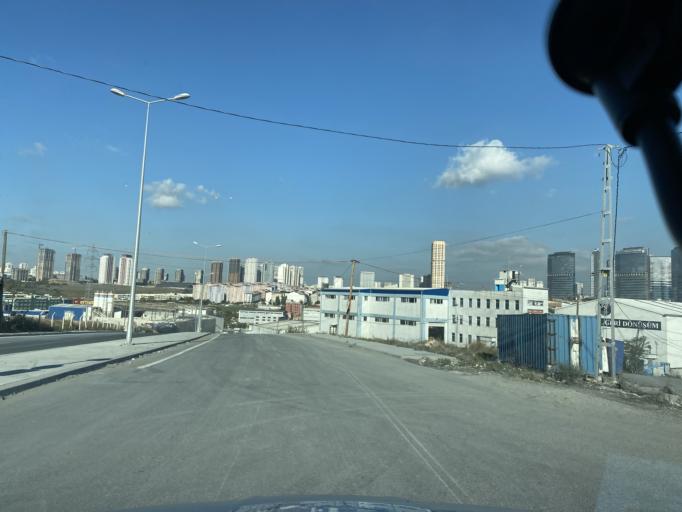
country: TR
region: Istanbul
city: Esenyurt
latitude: 41.0559
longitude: 28.6487
